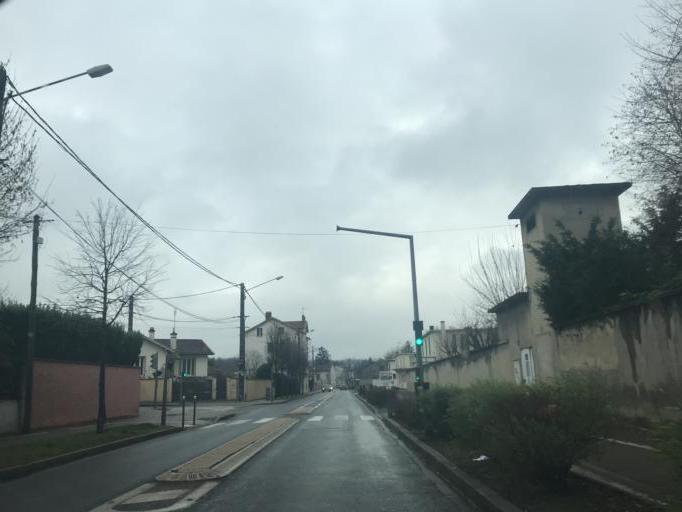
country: FR
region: Rhone-Alpes
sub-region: Departement du Rhone
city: Genay
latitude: 45.8870
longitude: 4.8307
